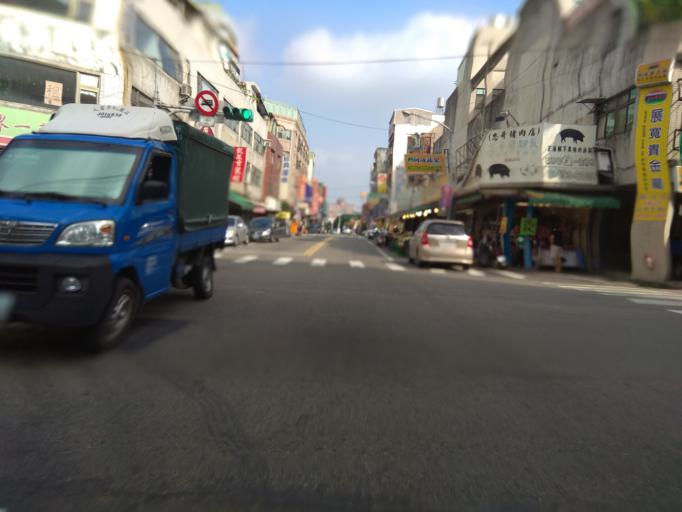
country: TW
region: Taiwan
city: Taoyuan City
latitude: 24.9565
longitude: 121.2180
